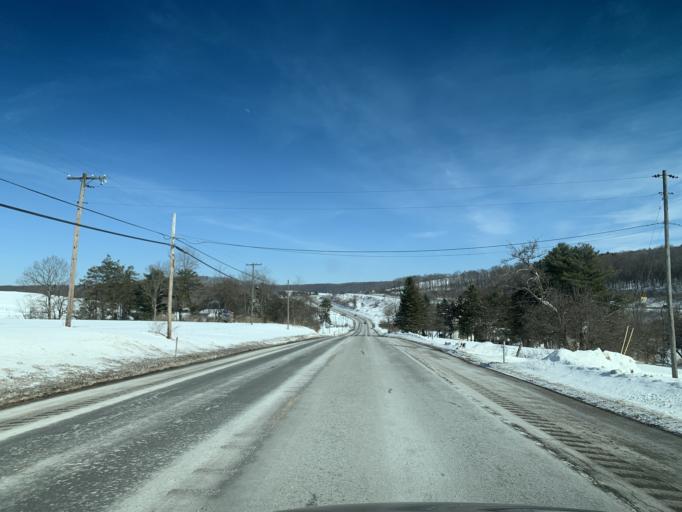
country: US
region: Maryland
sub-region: Allegany County
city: Frostburg
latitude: 39.6878
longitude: -78.9887
